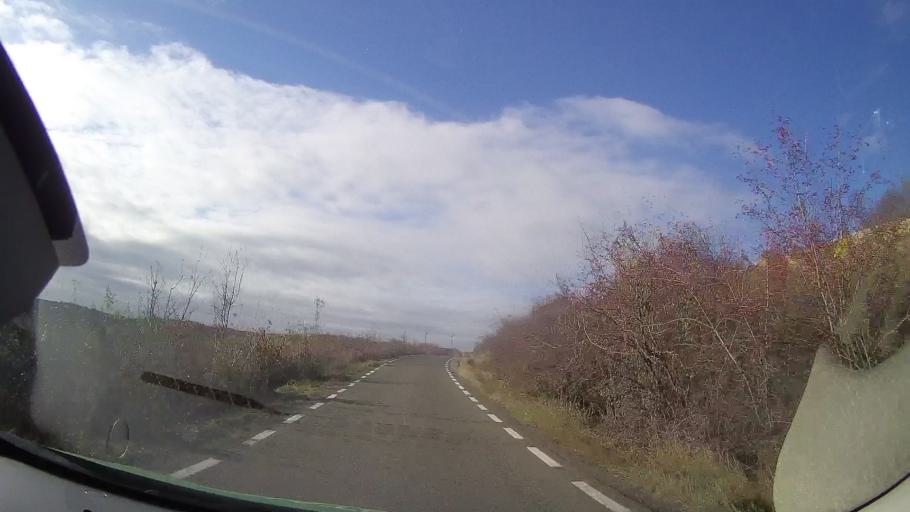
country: RO
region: Mures
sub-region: Comuna Sanger
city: Sanger
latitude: 46.5606
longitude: 24.1649
